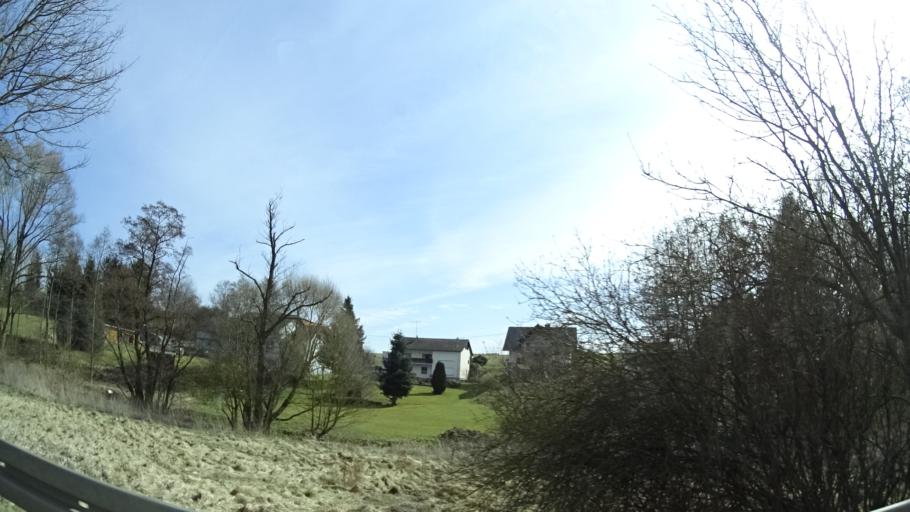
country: DE
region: Hesse
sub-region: Regierungsbezirk Giessen
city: Schwalmtal
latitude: 50.6667
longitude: 9.2749
